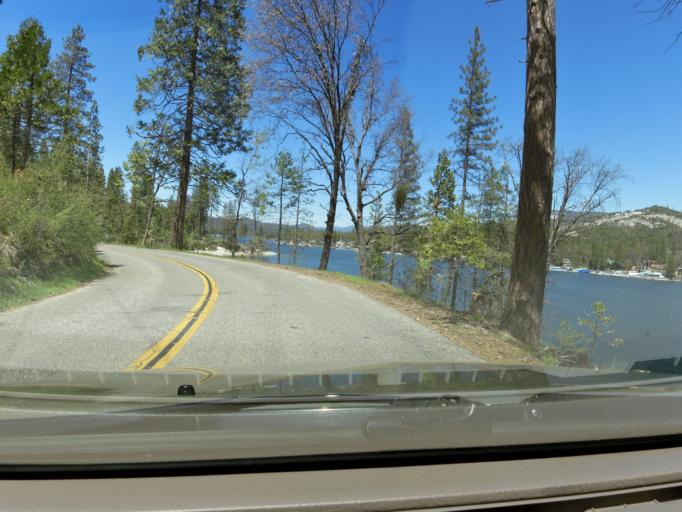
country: US
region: California
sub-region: Madera County
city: Oakhurst
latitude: 37.3134
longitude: -119.5576
